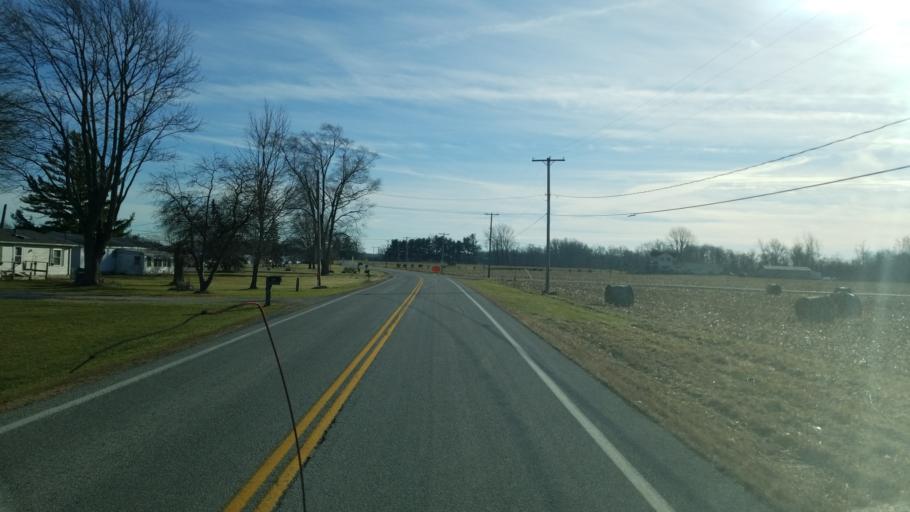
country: US
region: Ohio
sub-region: Sandusky County
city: Green Springs
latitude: 41.3078
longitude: -83.0536
